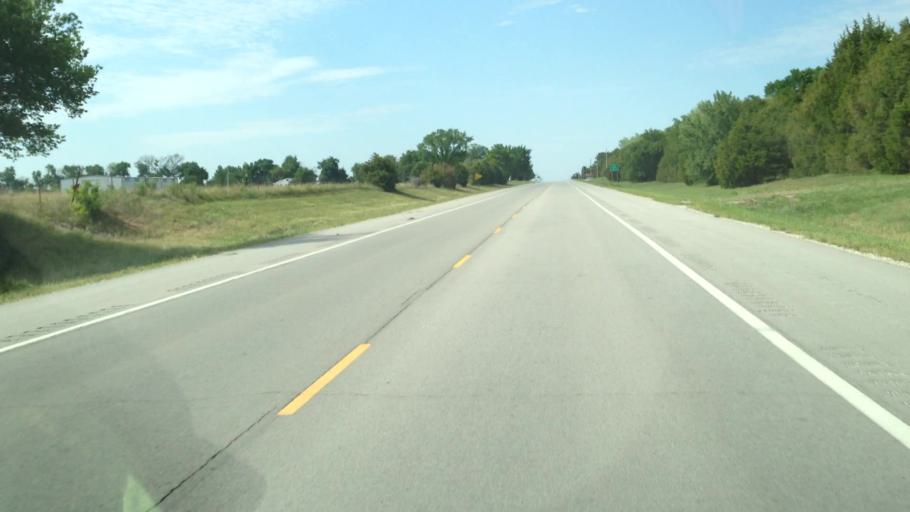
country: US
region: Kansas
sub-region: Labette County
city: Parsons
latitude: 37.3033
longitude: -95.2675
